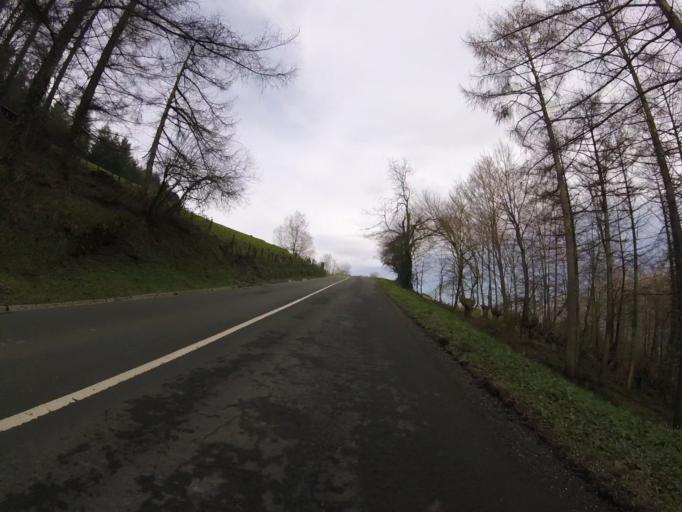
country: ES
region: Basque Country
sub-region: Provincia de Guipuzcoa
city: Errezil
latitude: 43.1479
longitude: -2.1838
